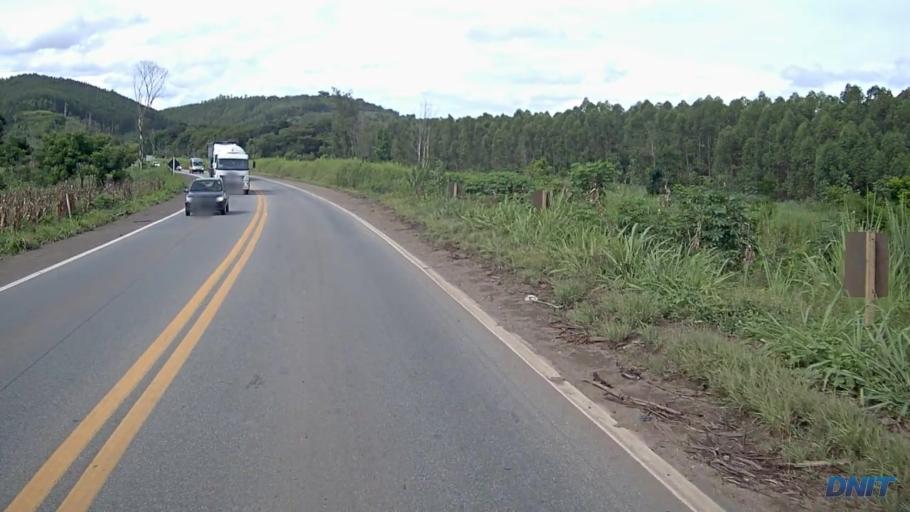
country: BR
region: Minas Gerais
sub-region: Ipaba
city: Ipaba
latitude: -19.3673
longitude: -42.4505
